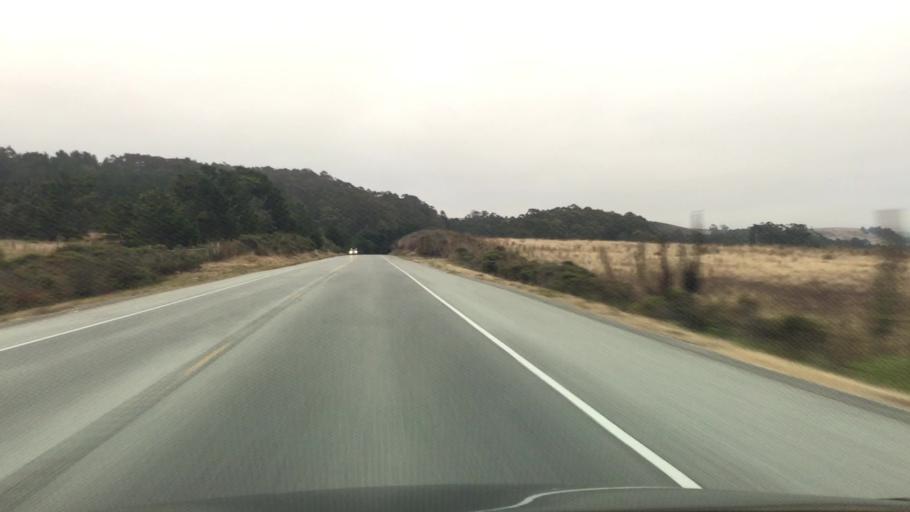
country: US
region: California
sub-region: San Mateo County
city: Half Moon Bay
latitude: 37.3913
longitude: -122.4096
